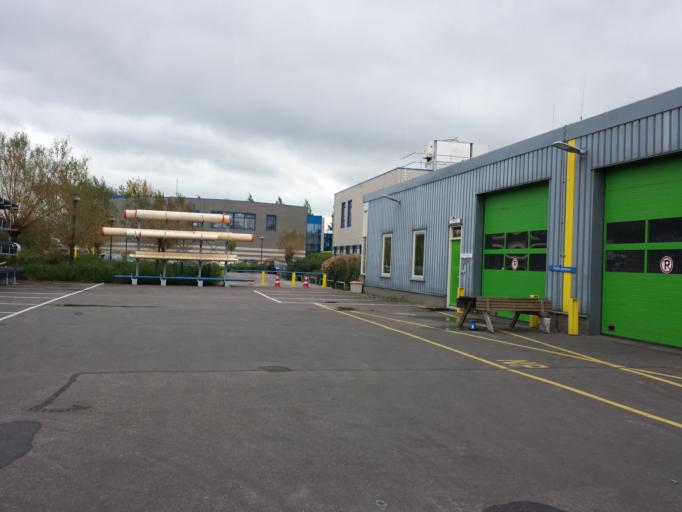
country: NL
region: South Holland
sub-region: Gemeente Gouda
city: Bloemendaal
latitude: 52.0168
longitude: 4.6906
